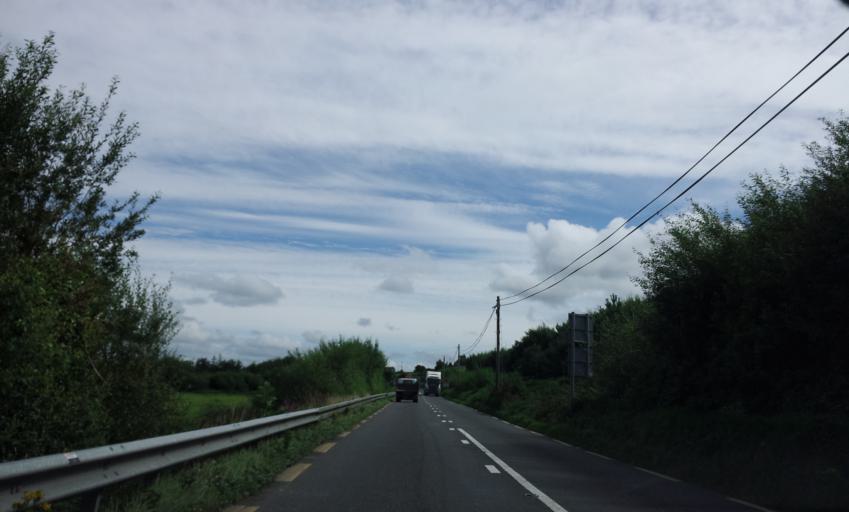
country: IE
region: Munster
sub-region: Ciarrai
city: Killorglin
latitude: 52.1037
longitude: -9.8111
